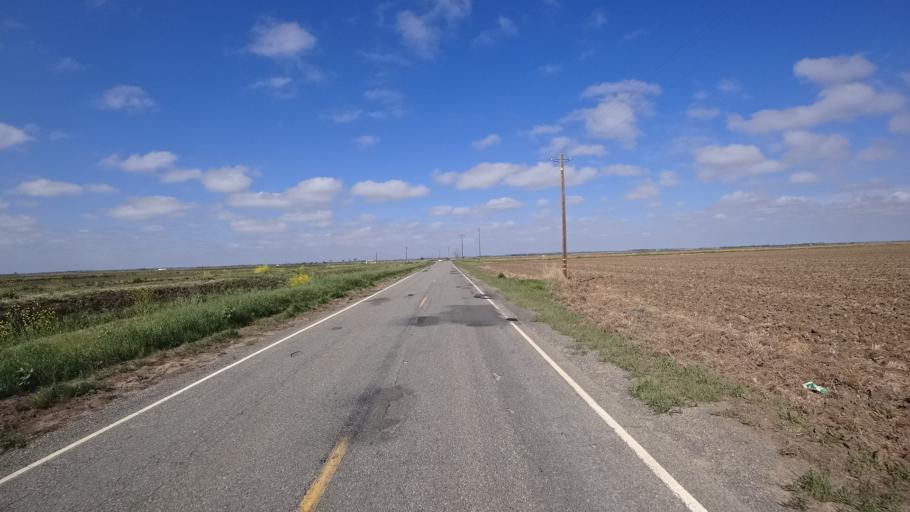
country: US
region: California
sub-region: Colusa County
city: Colusa
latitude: 39.3623
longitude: -121.9411
